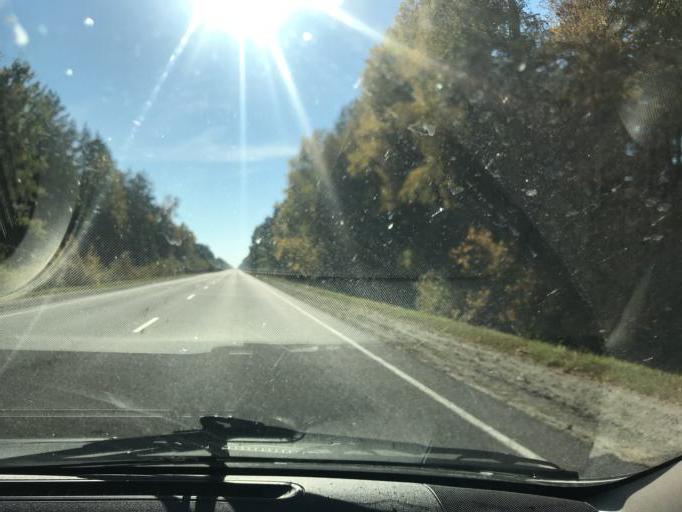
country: BY
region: Brest
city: Mikashevichy
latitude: 52.4540
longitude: 27.4725
